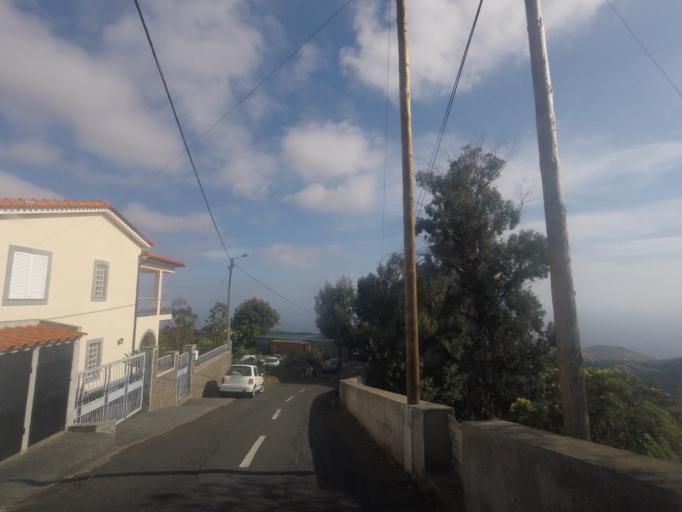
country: PT
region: Madeira
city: Camara de Lobos
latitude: 32.6772
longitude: -16.9539
